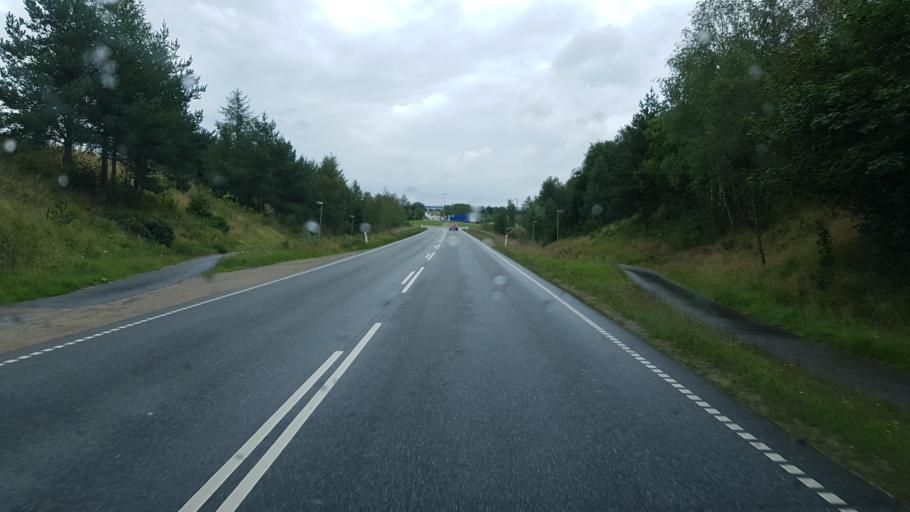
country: DK
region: Central Jutland
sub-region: Horsens Kommune
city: Horsens
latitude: 55.8989
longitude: 9.7502
